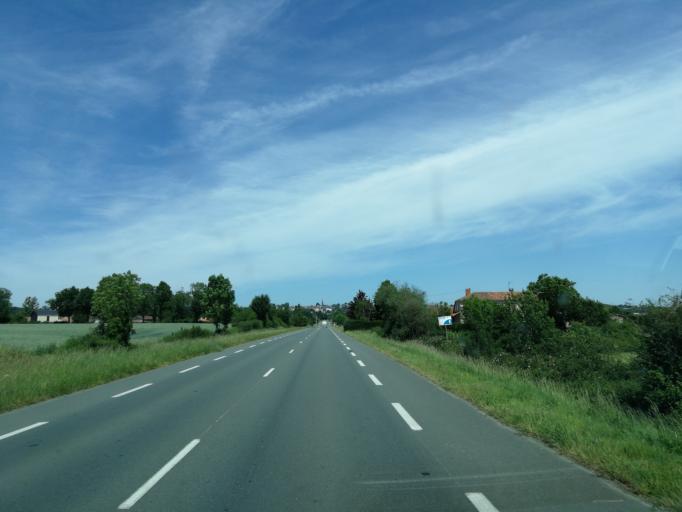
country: FR
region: Pays de la Loire
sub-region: Departement de la Vendee
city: Antigny
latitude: 46.6325
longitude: -0.7636
